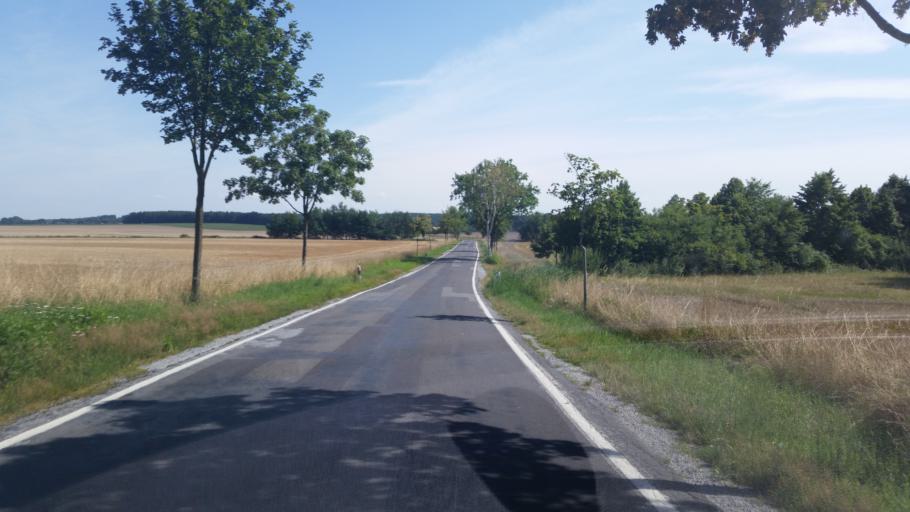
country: DE
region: Saxony
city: Schwepnitz
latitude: 51.3249
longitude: 14.0208
